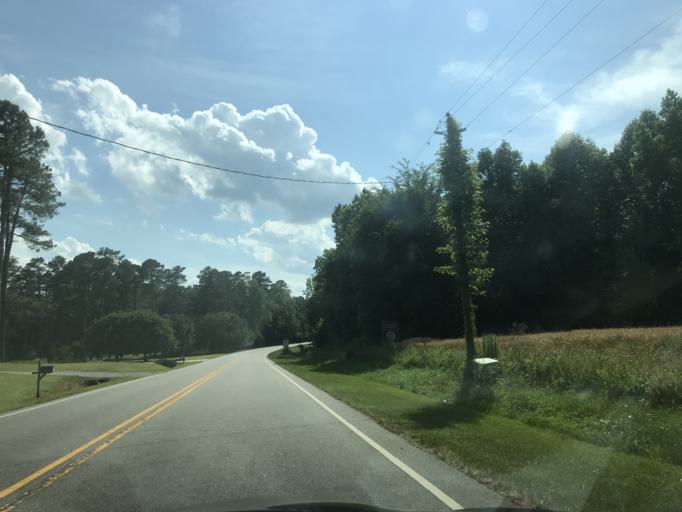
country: US
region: North Carolina
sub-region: Nash County
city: Nashville
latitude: 35.9692
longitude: -78.0209
